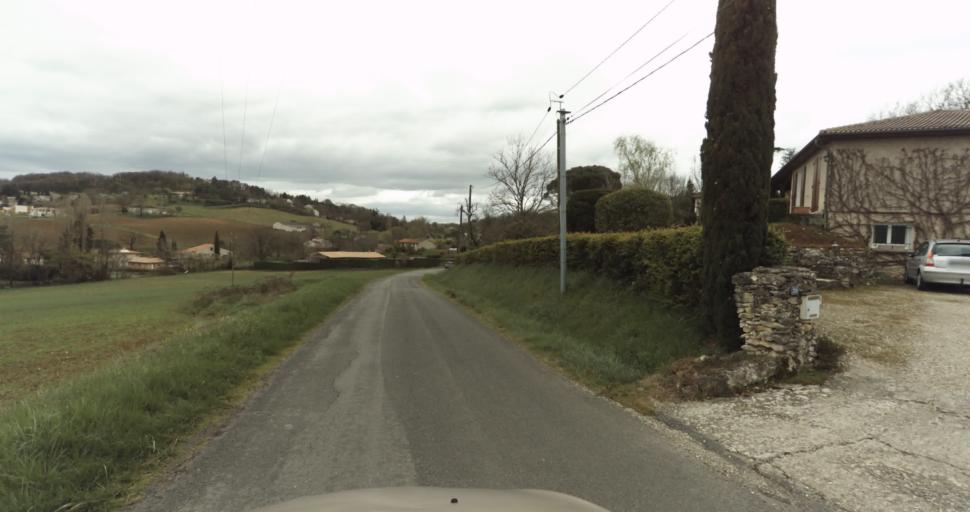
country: FR
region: Midi-Pyrenees
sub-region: Departement du Tarn
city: Puygouzon
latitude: 43.9068
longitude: 2.1669
